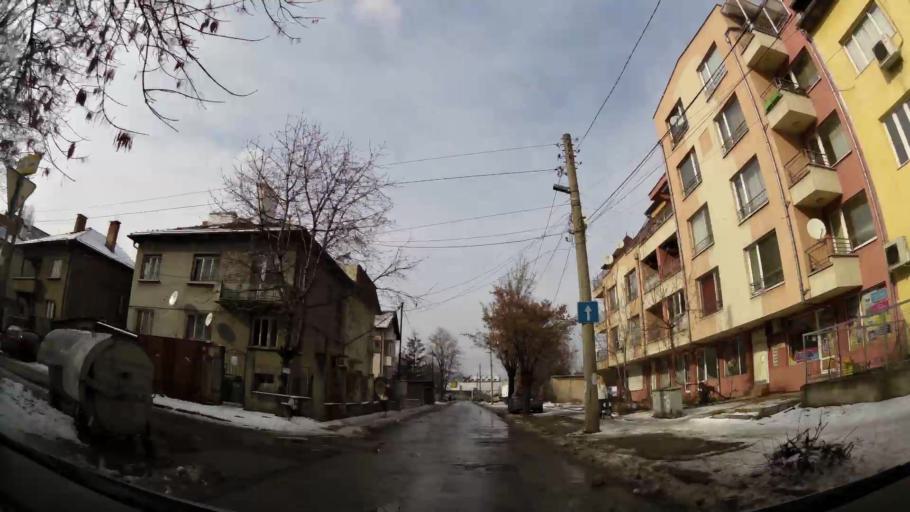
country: BG
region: Sofia-Capital
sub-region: Stolichna Obshtina
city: Sofia
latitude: 42.7073
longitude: 23.3445
